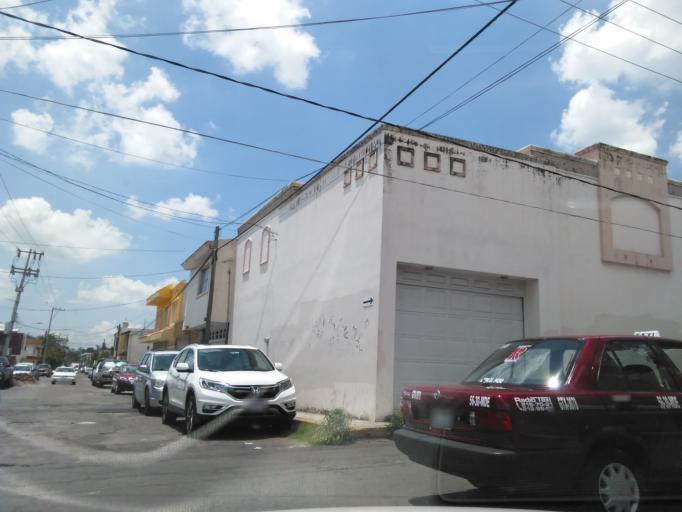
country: MX
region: Nayarit
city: Tepic
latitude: 21.5103
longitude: -104.9087
